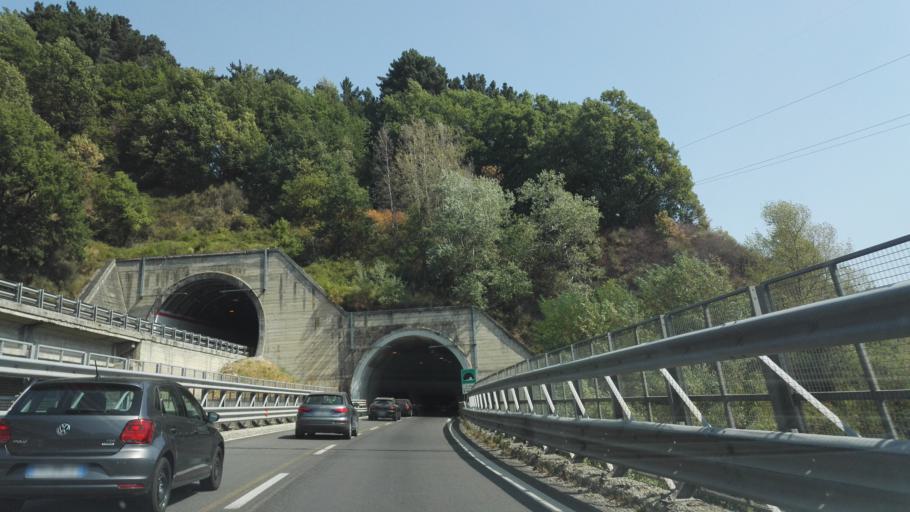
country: IT
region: Calabria
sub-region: Provincia di Cosenza
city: Belsito
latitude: 39.1747
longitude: 16.2940
